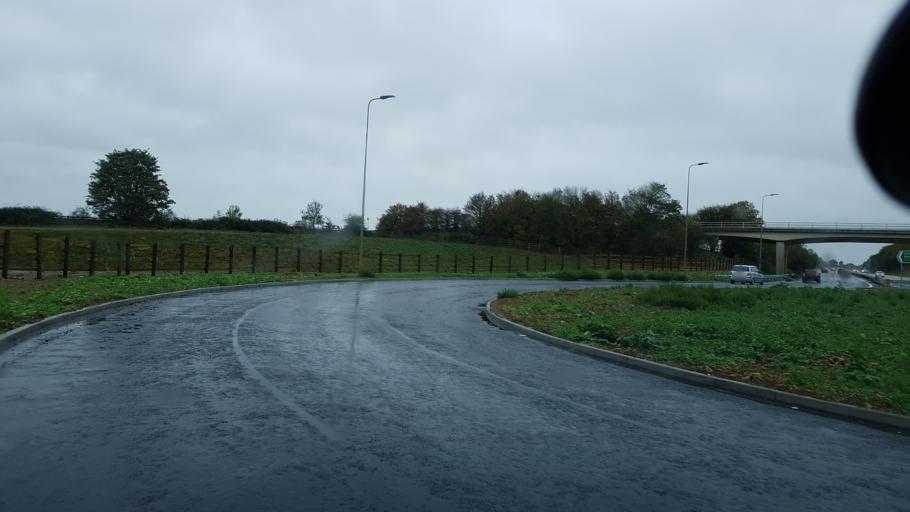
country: GB
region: England
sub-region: Oxfordshire
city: Witney
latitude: 51.7791
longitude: -1.5240
